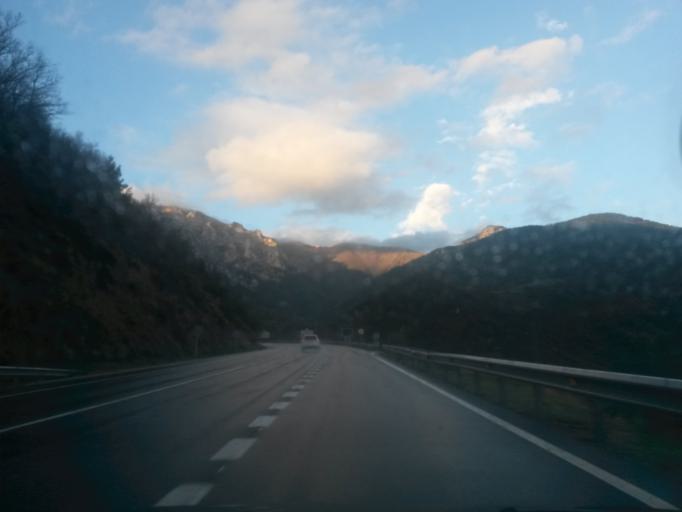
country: ES
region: Catalonia
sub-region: Provincia de Barcelona
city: Baga
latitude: 42.2898
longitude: 1.8565
